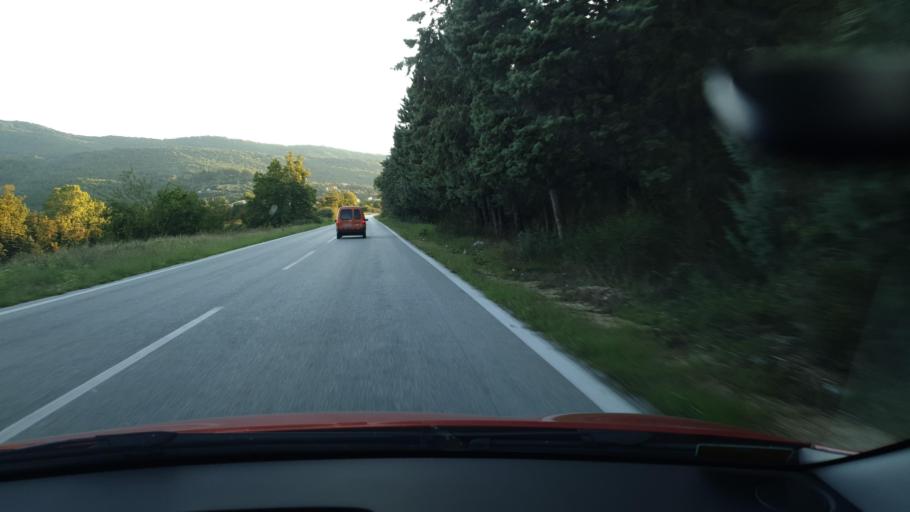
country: GR
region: Central Macedonia
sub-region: Nomos Thessalonikis
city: Nea Apollonia
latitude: 40.5060
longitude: 23.4612
